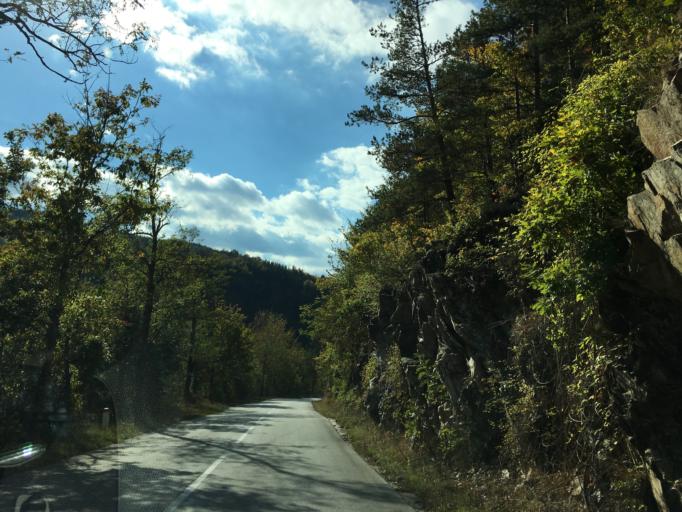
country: BG
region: Smolyan
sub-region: Obshtina Madan
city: Madan
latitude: 41.4592
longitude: 24.9742
